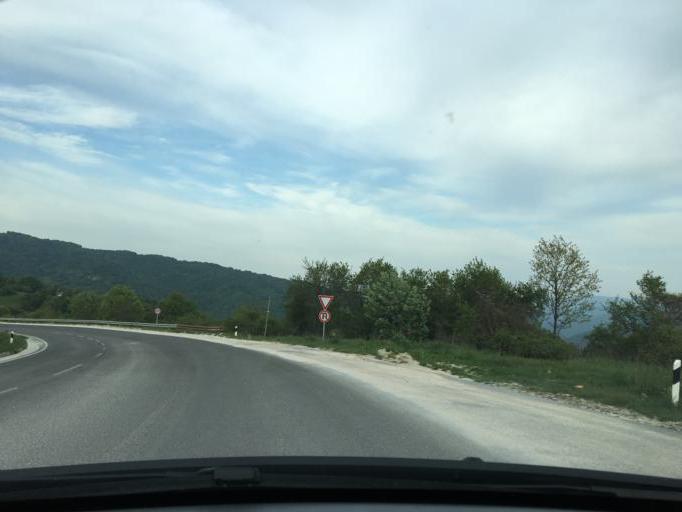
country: MK
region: Kriva Palanka
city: Kriva Palanka
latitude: 42.2183
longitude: 22.4530
